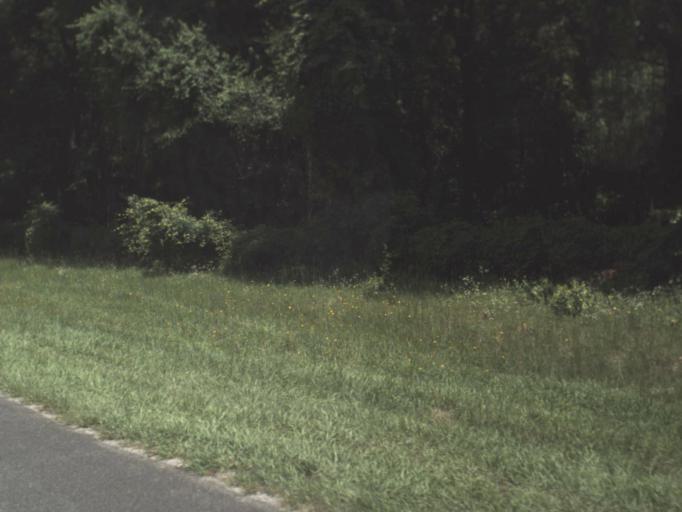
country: US
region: Florida
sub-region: Alachua County
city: High Springs
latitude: 29.8517
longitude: -82.6404
